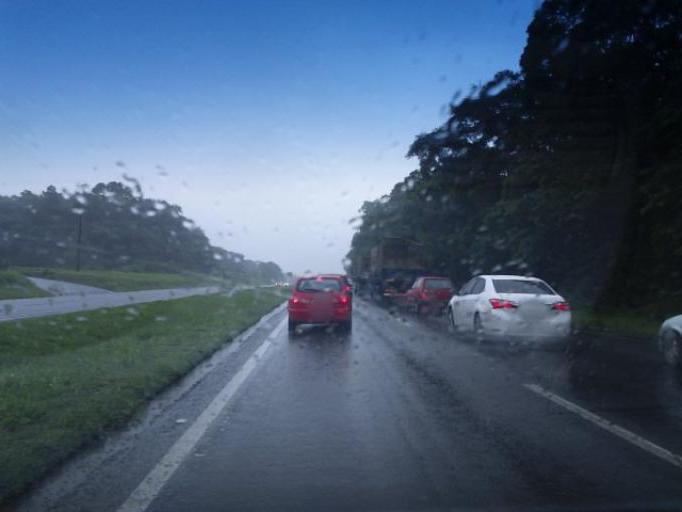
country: BR
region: Santa Catarina
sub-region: Joinville
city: Joinville
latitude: -26.0258
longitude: -48.8614
